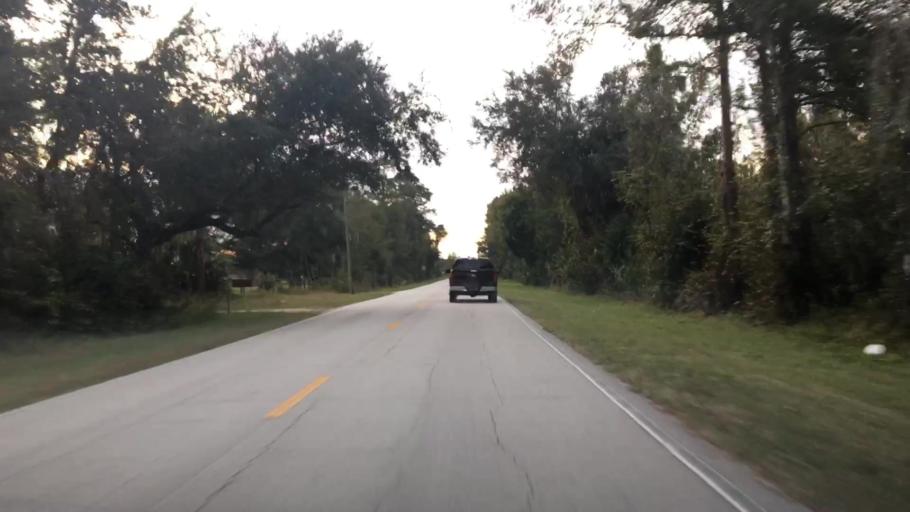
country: US
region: Florida
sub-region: Seminole County
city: Midway
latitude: 28.8426
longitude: -81.1972
